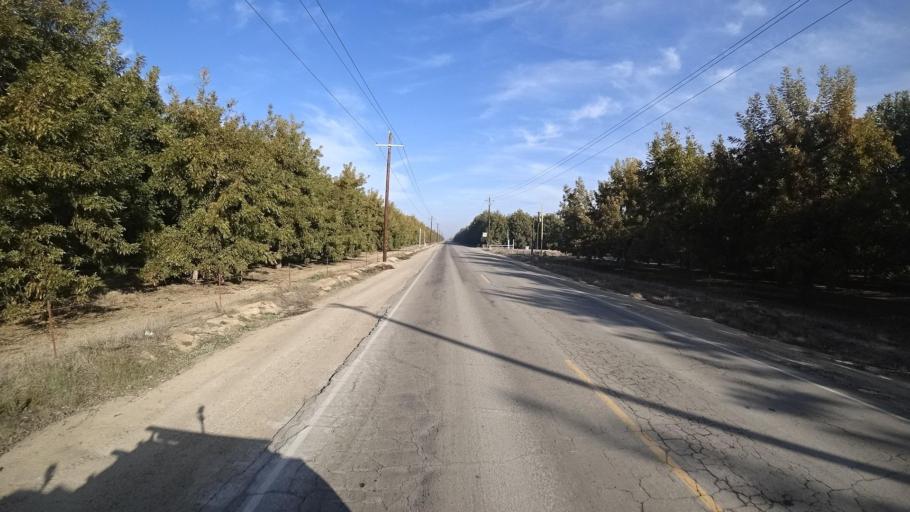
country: US
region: California
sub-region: Kern County
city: McFarland
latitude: 35.6212
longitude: -119.2044
